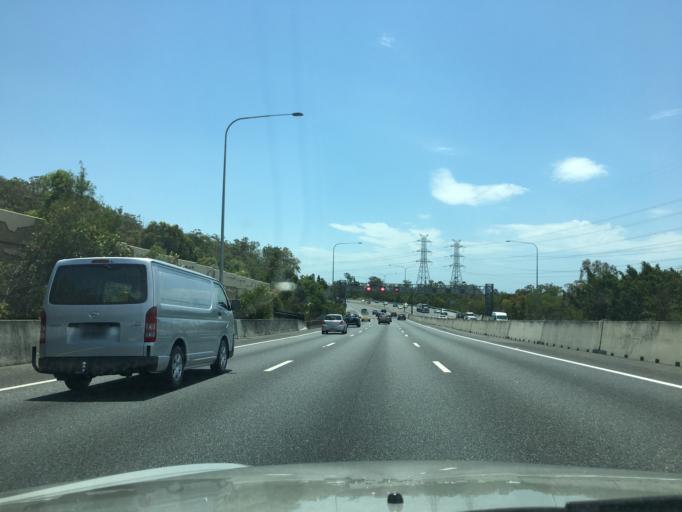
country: AU
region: Queensland
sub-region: Brisbane
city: Belmont
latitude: -27.5146
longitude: 153.1256
